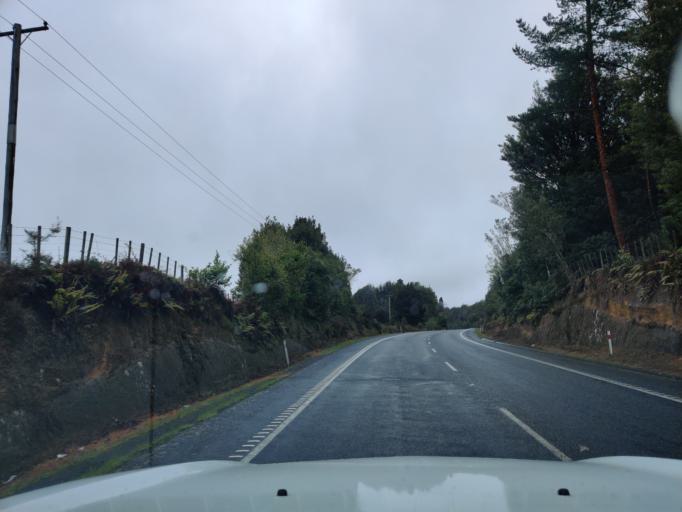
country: NZ
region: Bay of Plenty
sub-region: Rotorua District
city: Rotorua
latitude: -38.0603
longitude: 176.0938
